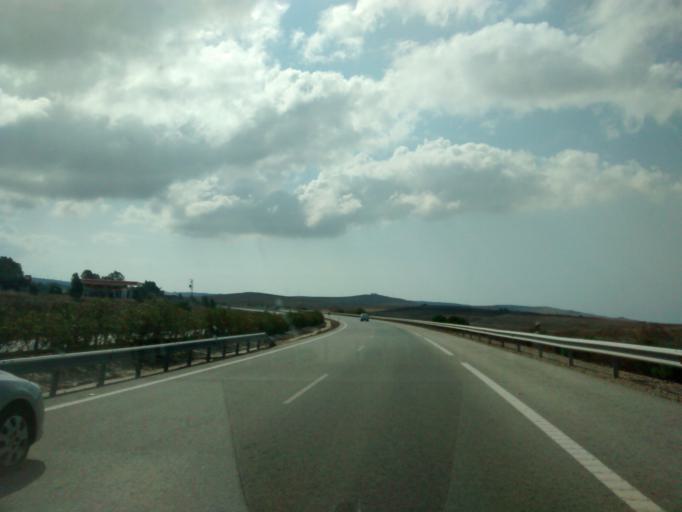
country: ES
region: Andalusia
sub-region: Provincia de Cadiz
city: Vejer de la Frontera
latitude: 36.2549
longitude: -6.0276
